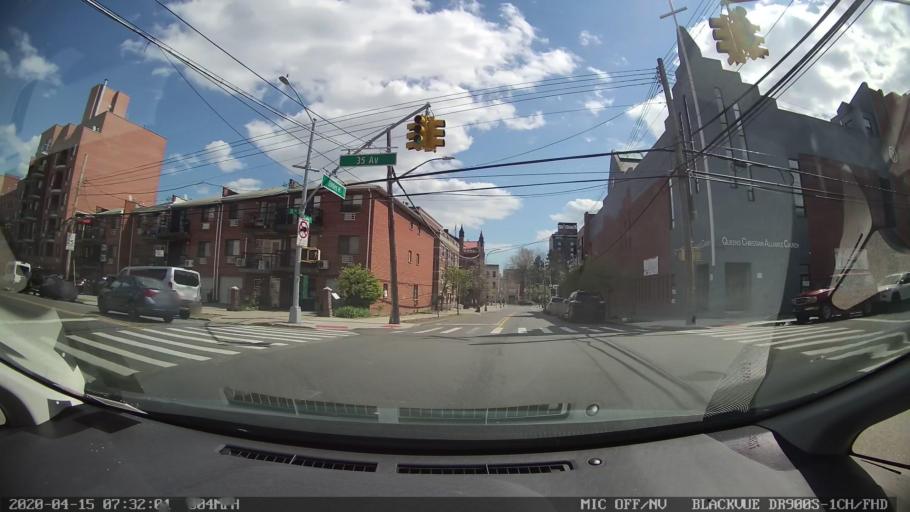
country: US
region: New York
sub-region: Queens County
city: Jamaica
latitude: 40.7648
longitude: -73.8307
